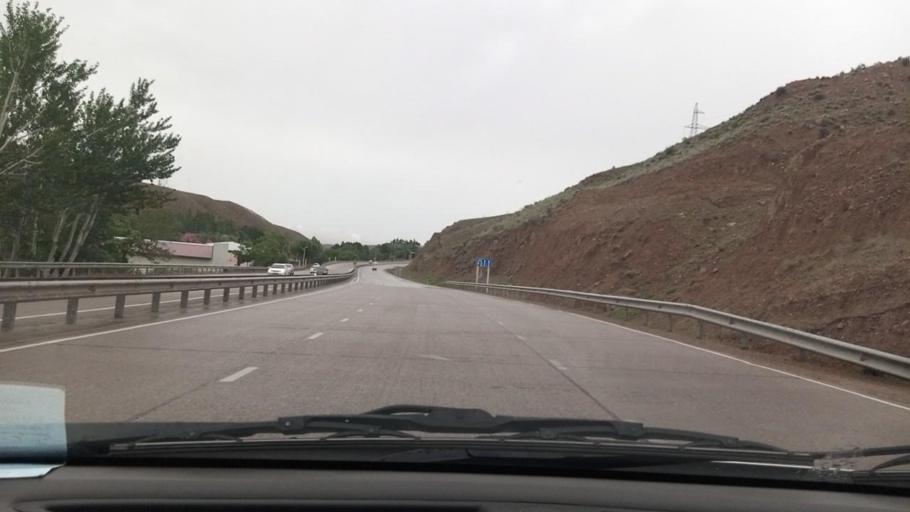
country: TJ
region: Viloyati Sughd
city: Shaydon
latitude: 40.9516
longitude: 70.6766
